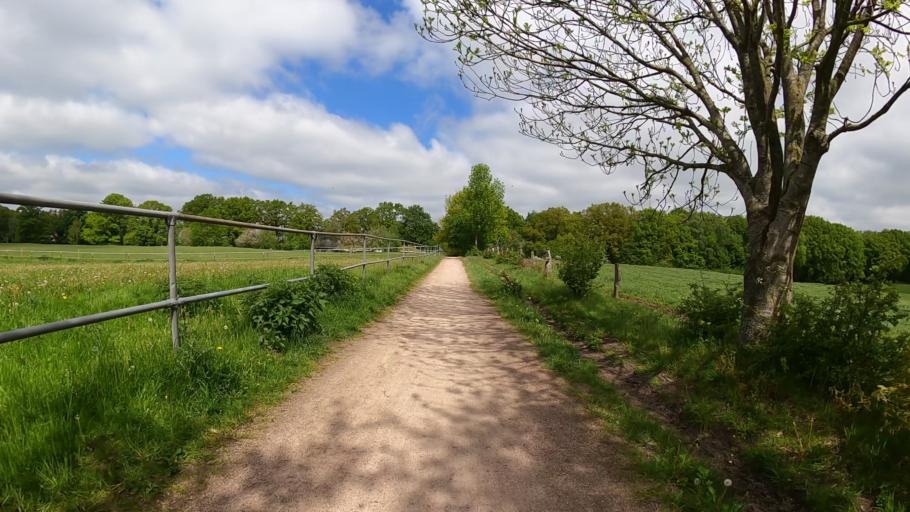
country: DE
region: Hamburg
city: Wohldorf-Ohlstedt
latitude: 53.7129
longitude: 10.1410
